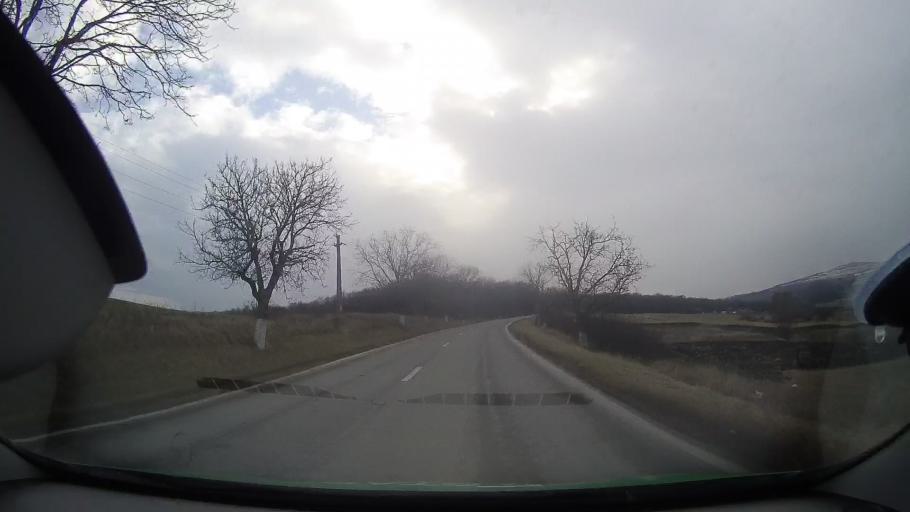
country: RO
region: Mures
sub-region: Municipiul Tarnaveni
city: Bobohalma
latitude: 46.3543
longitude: 24.2669
